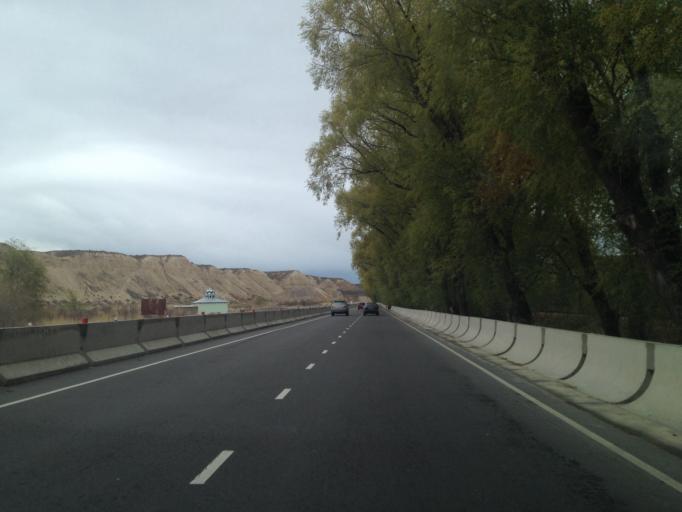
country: KG
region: Ysyk-Koel
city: Balykchy
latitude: 42.4678
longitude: 75.9048
